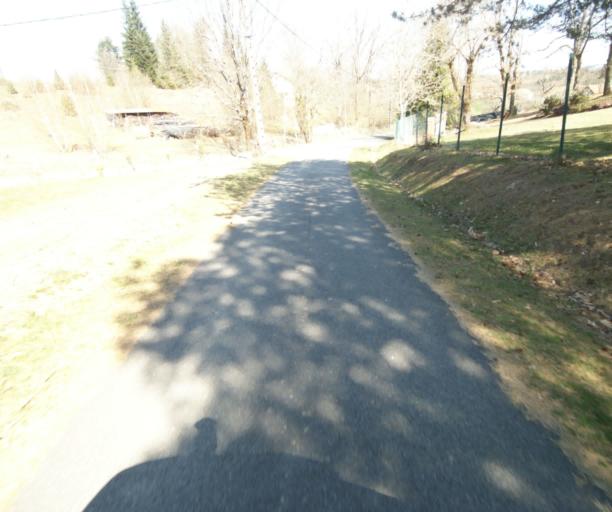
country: FR
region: Limousin
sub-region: Departement de la Correze
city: Saint-Mexant
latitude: 45.2757
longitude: 1.6612
